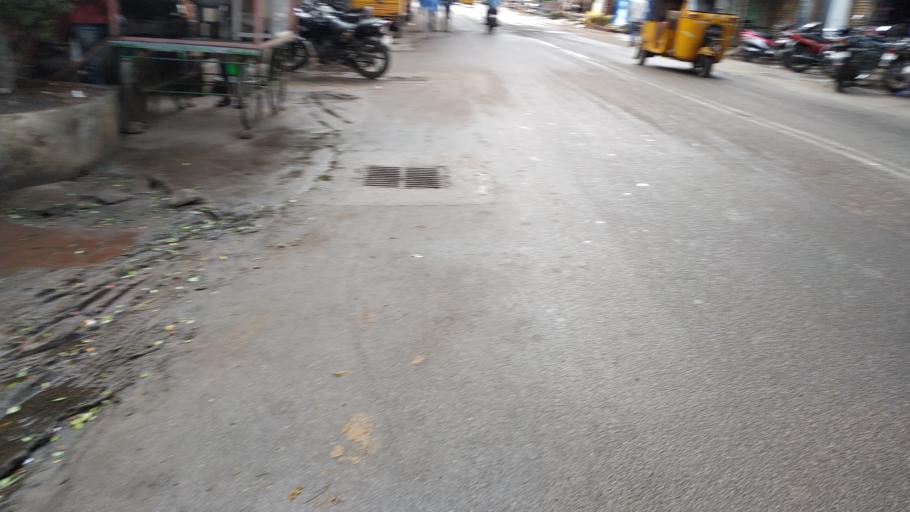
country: IN
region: Telangana
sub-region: Hyderabad
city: Malkajgiri
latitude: 17.4243
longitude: 78.5160
